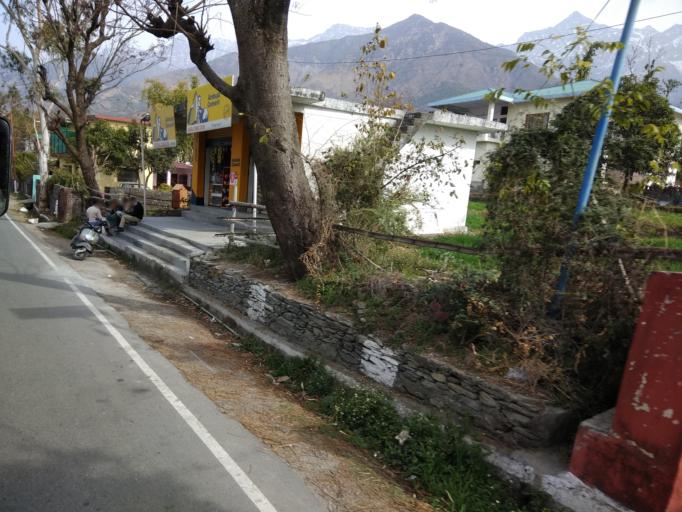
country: IN
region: Himachal Pradesh
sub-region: Kangra
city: Dharmsala
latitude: 32.1689
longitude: 76.3910
